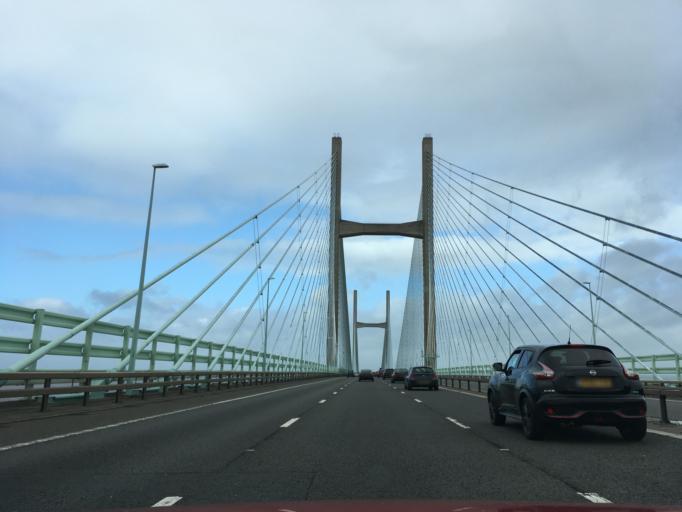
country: GB
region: England
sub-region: South Gloucestershire
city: Severn Beach
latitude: 51.5725
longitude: -2.6935
